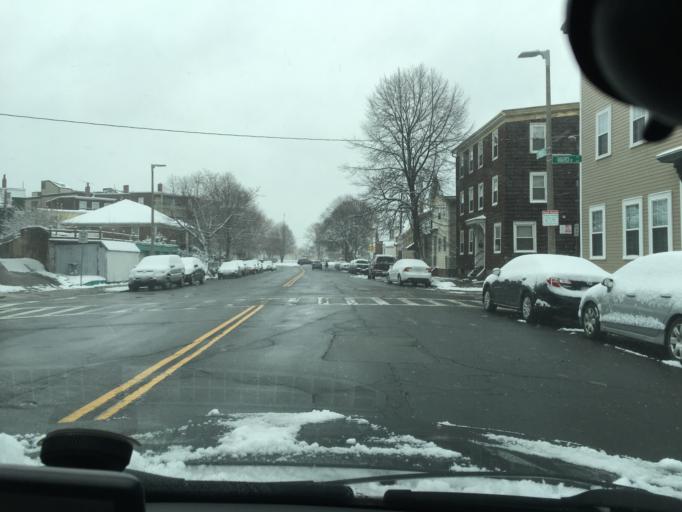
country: US
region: Massachusetts
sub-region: Suffolk County
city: South Boston
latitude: 42.3292
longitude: -71.0547
